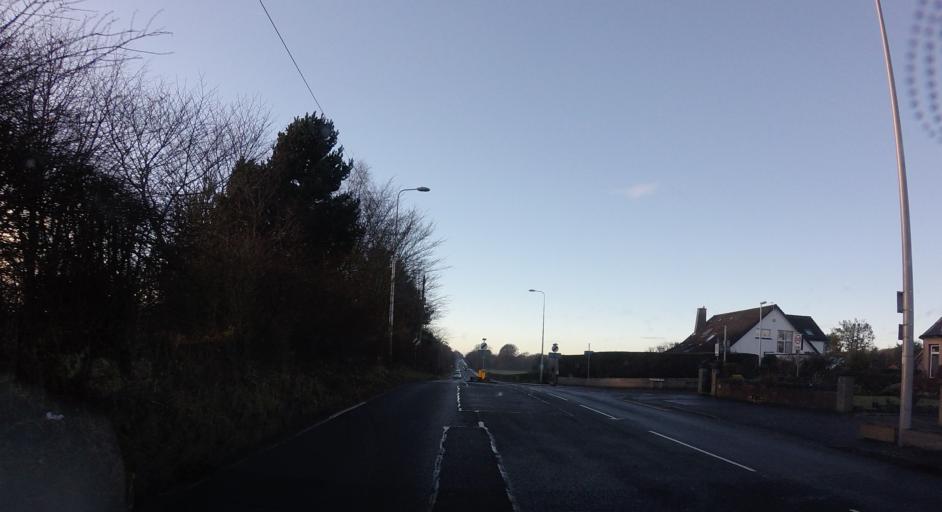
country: GB
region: Scotland
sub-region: Fife
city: Crossford
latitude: 56.0626
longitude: -3.5057
